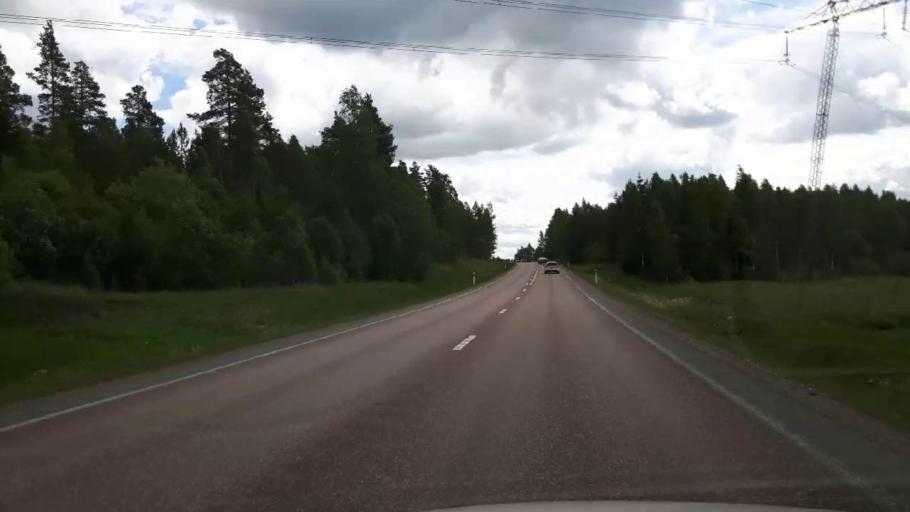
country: SE
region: Dalarna
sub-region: Saters Kommun
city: Saeter
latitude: 60.4866
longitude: 15.7683
